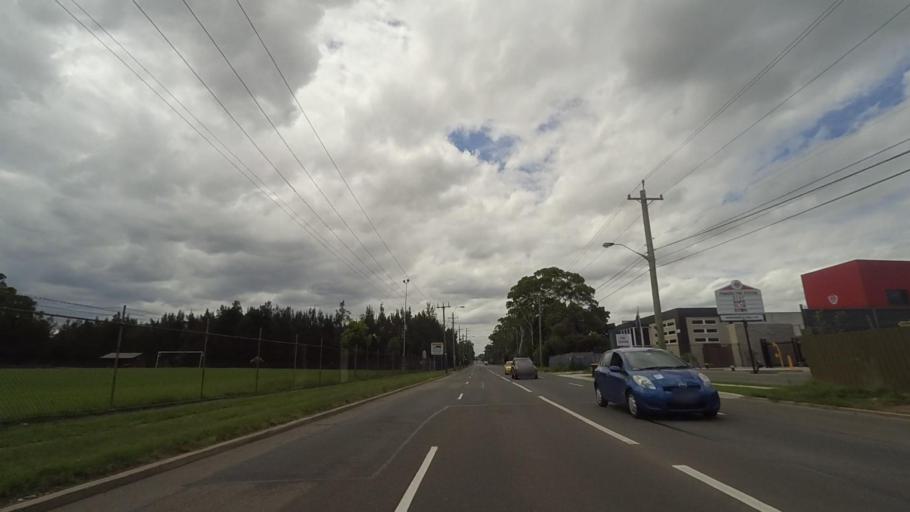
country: AU
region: New South Wales
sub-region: Fairfield
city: Fairfield East
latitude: -33.8590
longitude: 150.9582
